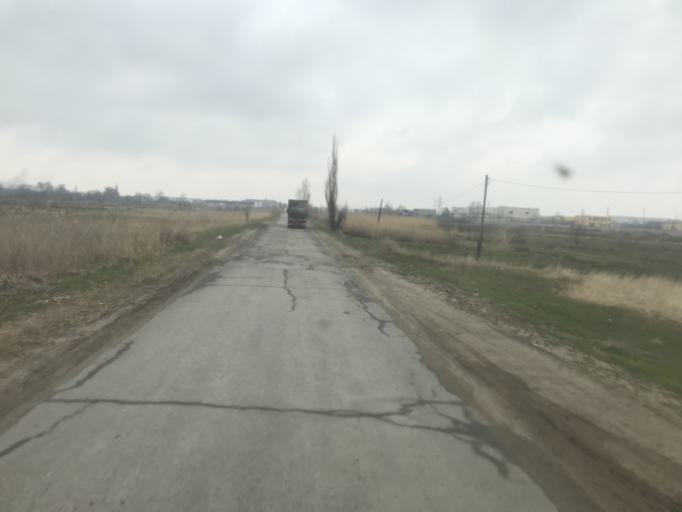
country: RU
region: Volgograd
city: Svetlyy Yar
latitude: 48.5193
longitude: 44.6258
